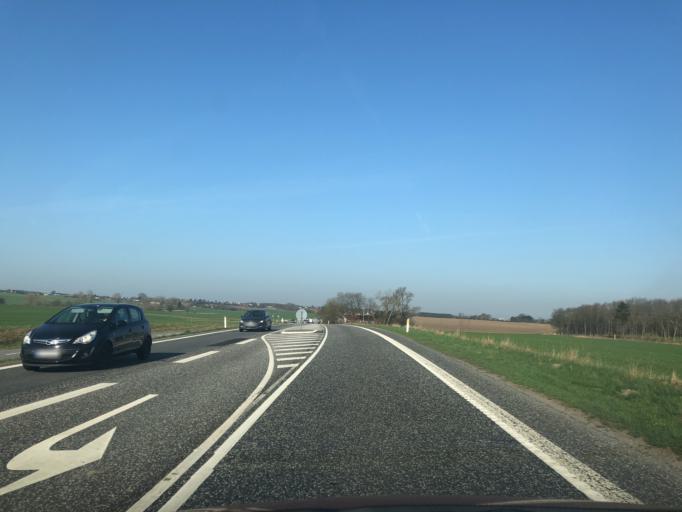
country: DK
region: Zealand
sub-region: Faxe Kommune
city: Ronnede
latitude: 55.2562
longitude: 12.0625
